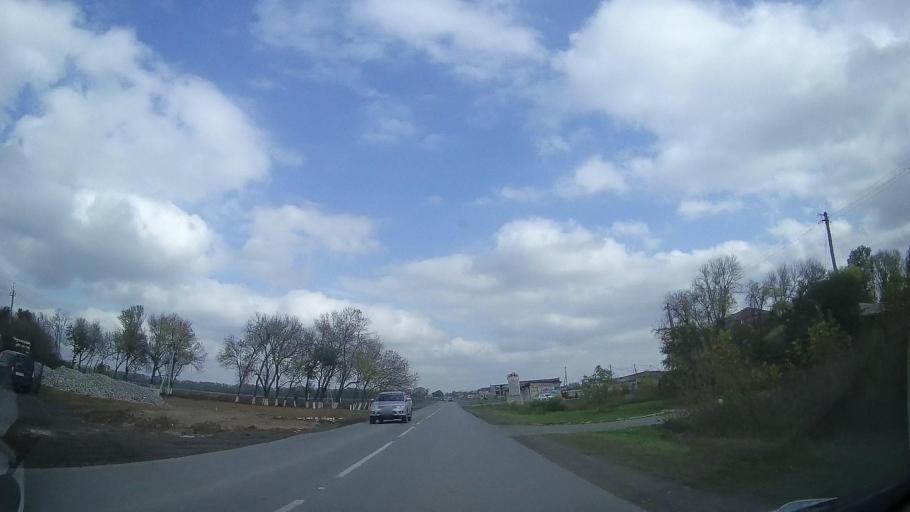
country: RU
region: Rostov
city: Severnyy
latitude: 47.2914
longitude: 39.6386
